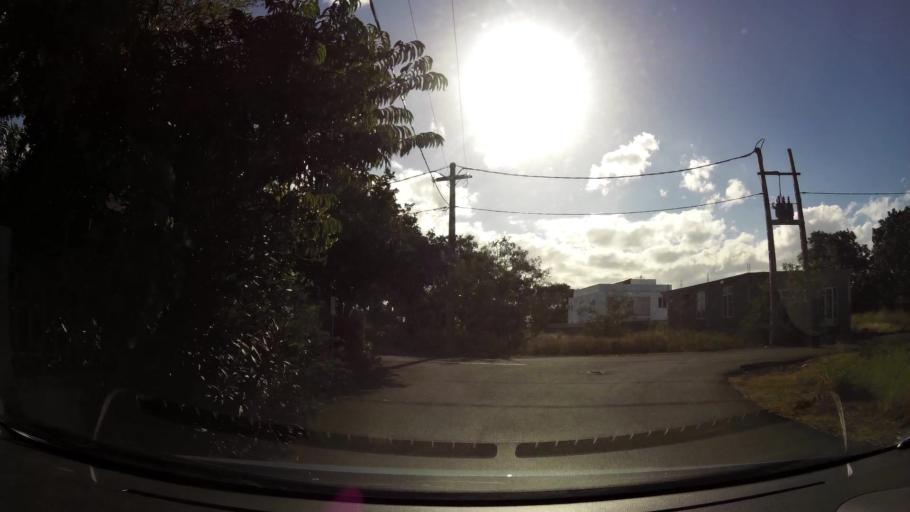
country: MU
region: Black River
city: Albion
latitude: -20.1972
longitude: 57.4098
